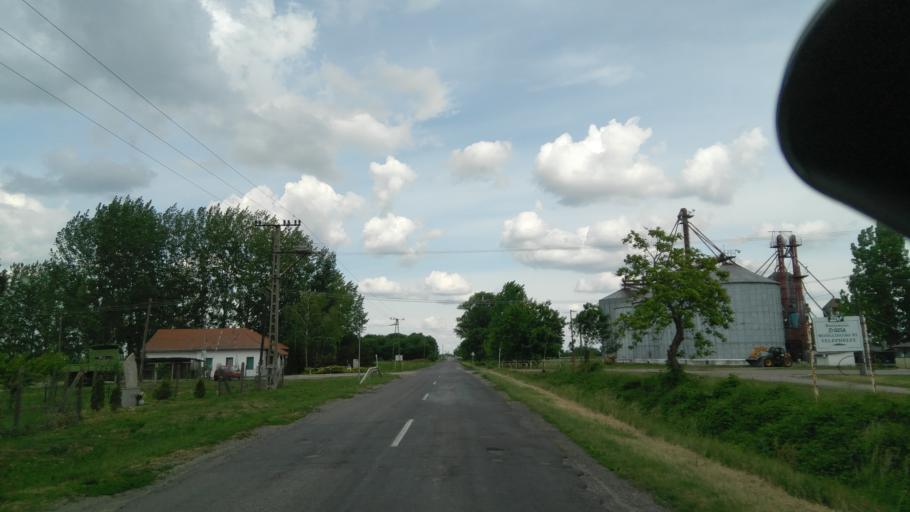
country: HU
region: Bekes
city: Battonya
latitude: 46.2938
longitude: 20.9790
